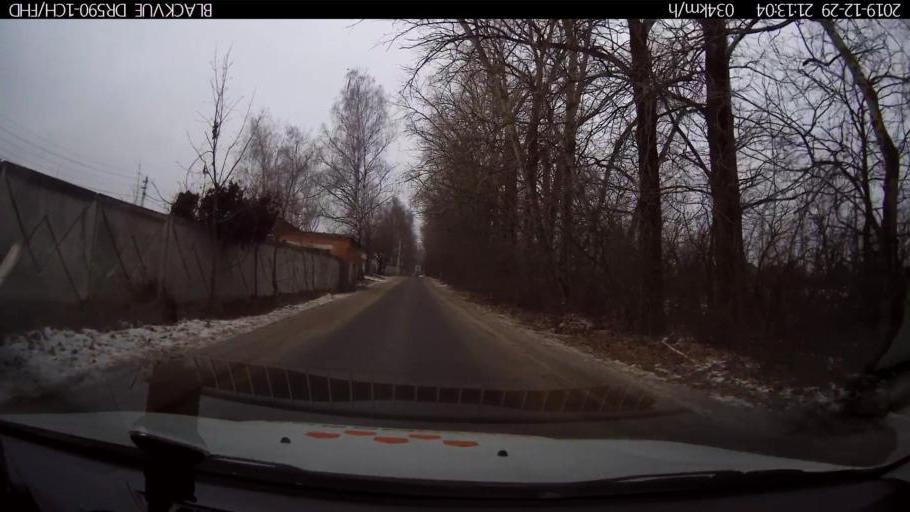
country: RU
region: Nizjnij Novgorod
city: Afonino
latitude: 56.2210
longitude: 44.0379
